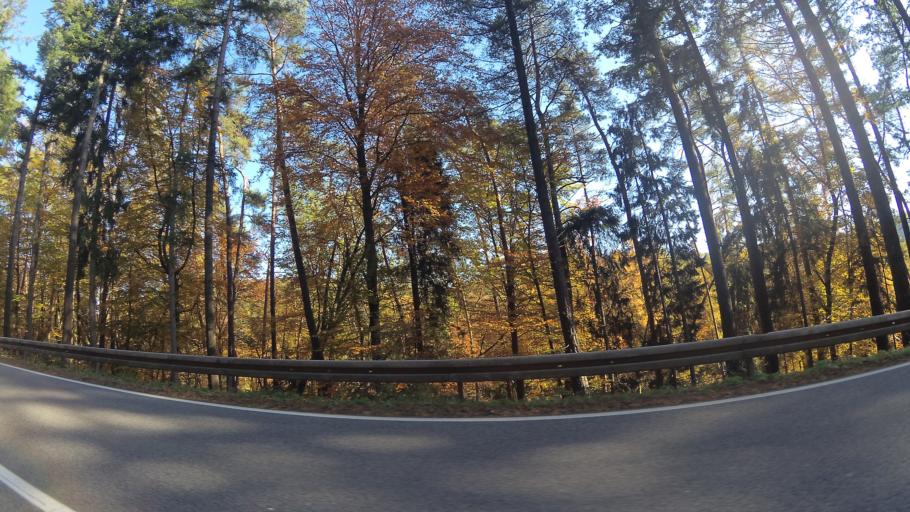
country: DE
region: Saarland
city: Losheim
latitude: 49.4977
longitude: 6.7285
